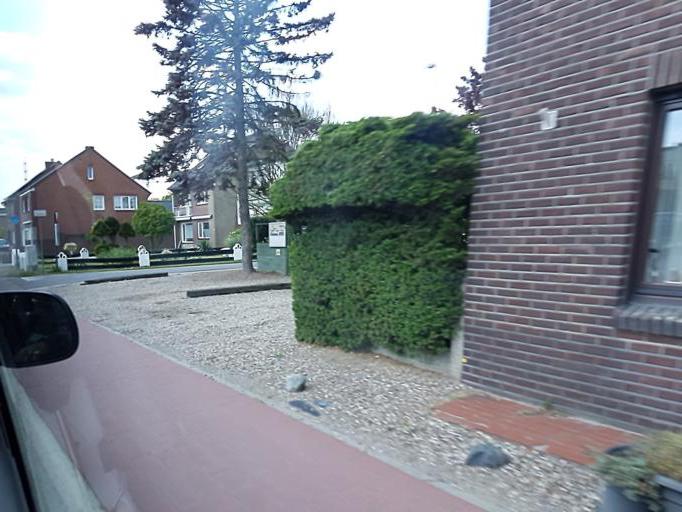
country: BE
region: Flanders
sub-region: Provincie Limburg
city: Neerpelt
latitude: 51.2284
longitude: 5.4768
